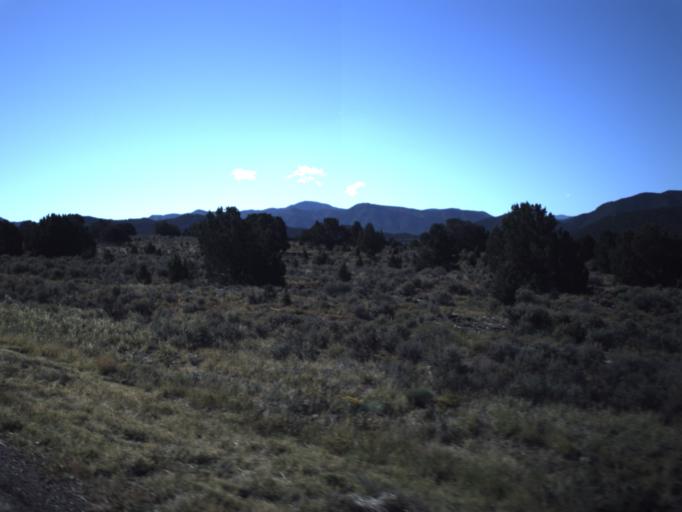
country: US
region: Utah
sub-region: Washington County
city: Enterprise
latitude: 37.6371
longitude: -113.4339
